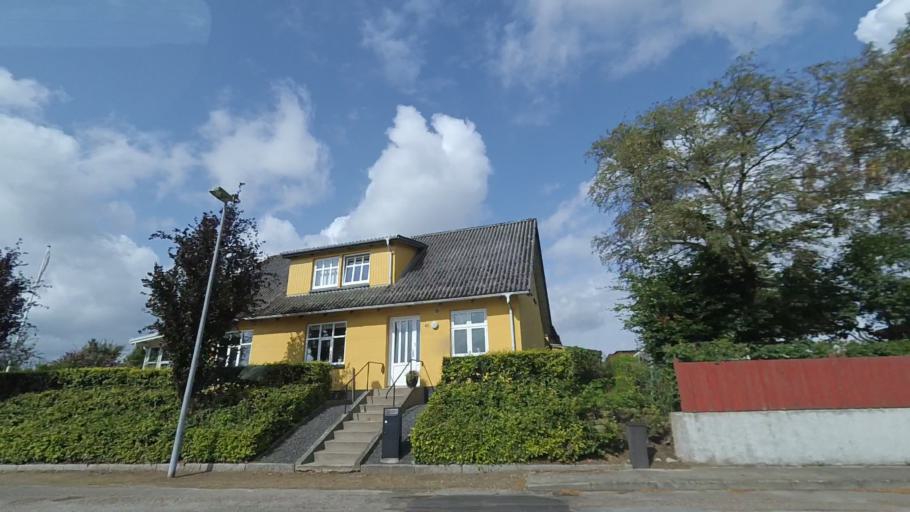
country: DK
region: Central Jutland
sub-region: Syddjurs Kommune
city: Ryomgard
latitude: 56.4767
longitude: 10.5070
